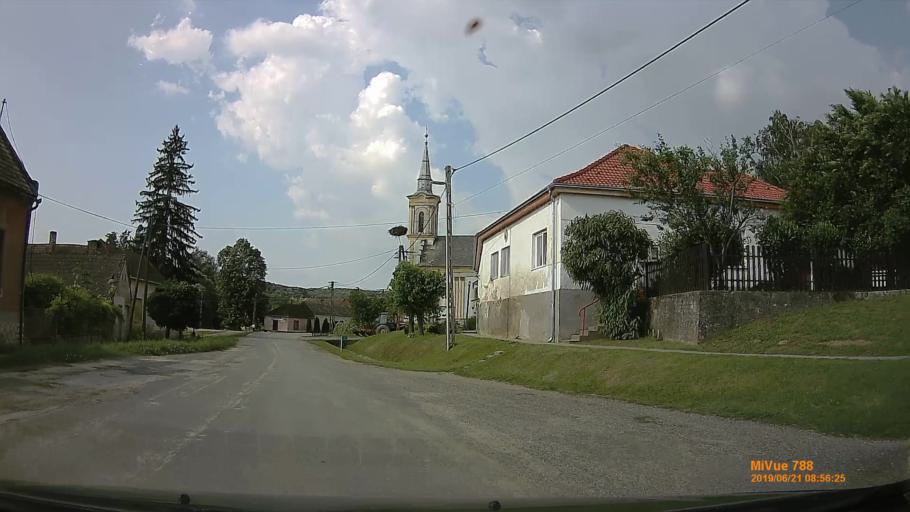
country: HU
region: Baranya
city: Buekkoesd
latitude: 46.1575
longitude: 17.8745
